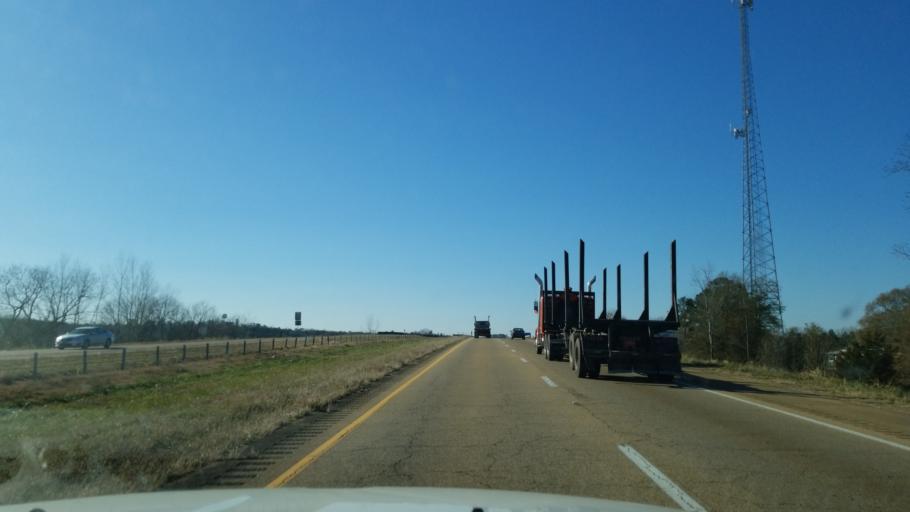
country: US
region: Mississippi
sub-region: Oktibbeha County
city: Starkville
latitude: 33.4692
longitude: -88.7518
